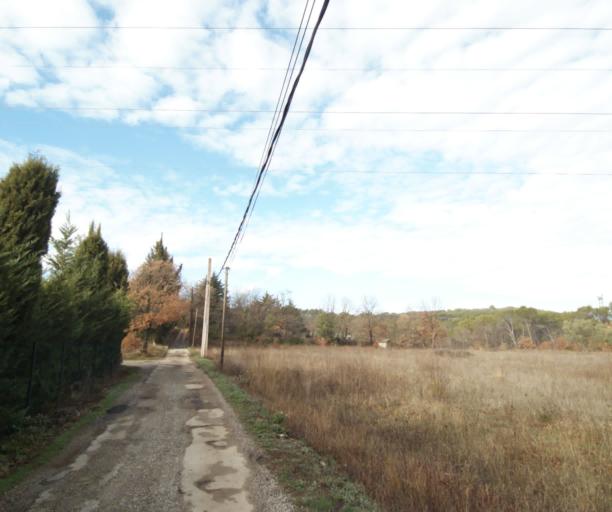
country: FR
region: Provence-Alpes-Cote d'Azur
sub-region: Departement du Var
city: Trans-en-Provence
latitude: 43.5061
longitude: 6.4743
